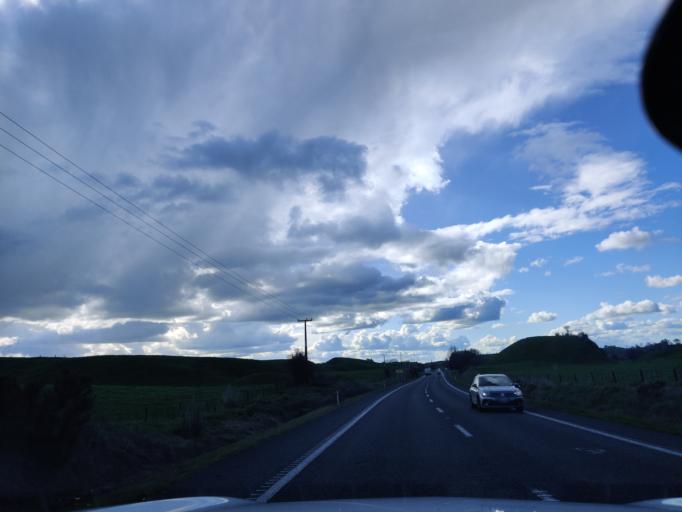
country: NZ
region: Waikato
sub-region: South Waikato District
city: Tokoroa
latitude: -38.1551
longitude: 175.8525
